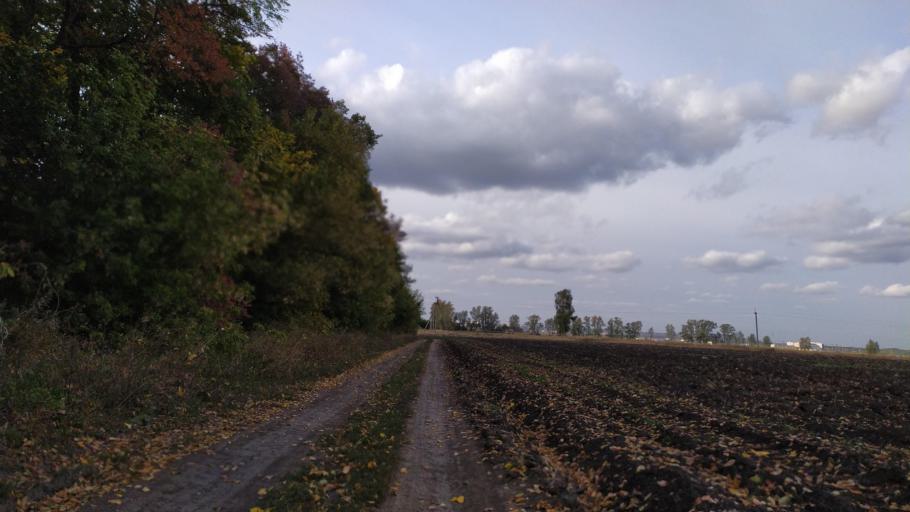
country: RU
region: Kursk
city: Kursk
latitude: 51.6235
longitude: 36.1613
